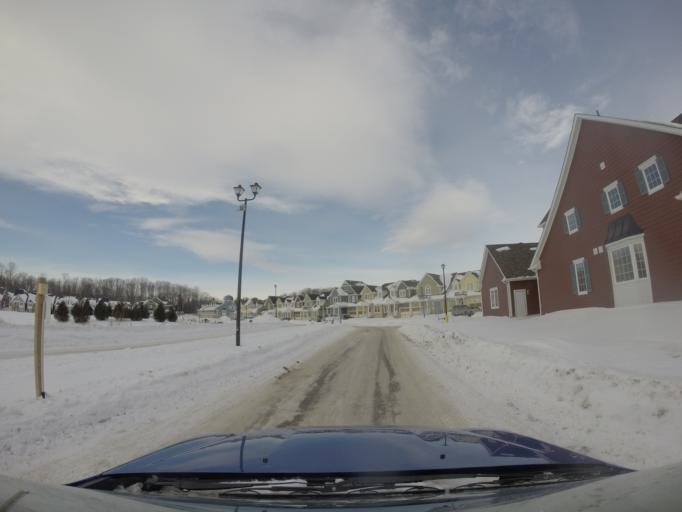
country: CA
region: Ontario
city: Wasaga Beach
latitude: 44.5308
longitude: -79.9833
